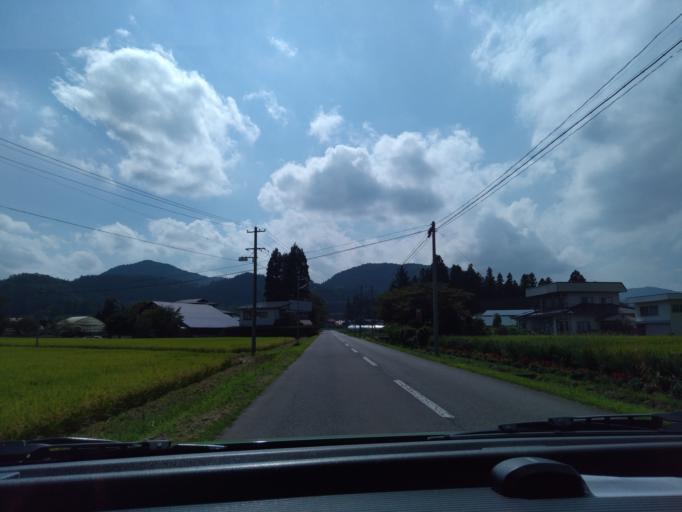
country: JP
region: Iwate
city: Shizukuishi
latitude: 39.6843
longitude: 140.9252
